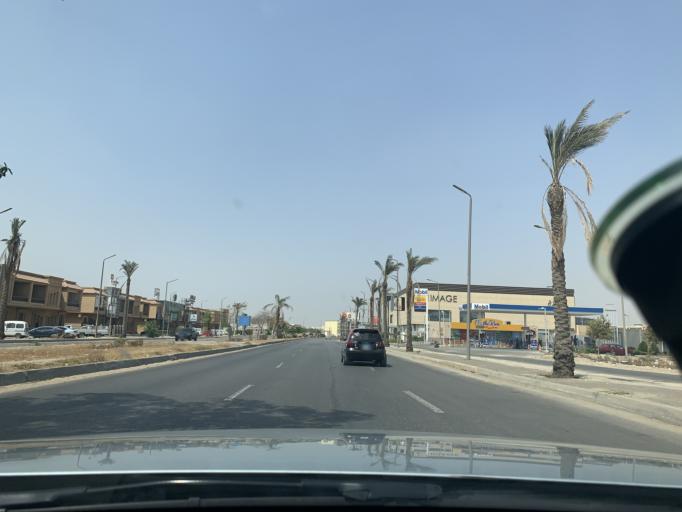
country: EG
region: Muhafazat al Qahirah
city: Cairo
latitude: 30.0884
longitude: 31.3681
